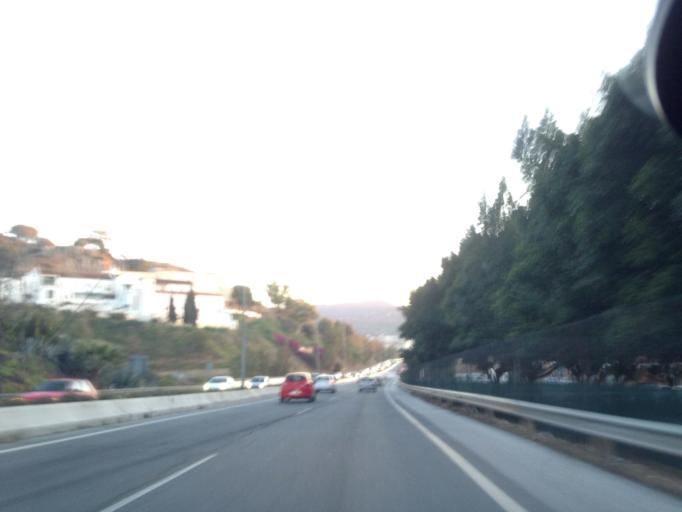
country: ES
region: Andalusia
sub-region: Provincia de Malaga
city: Malaga
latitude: 36.7311
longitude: -4.4419
